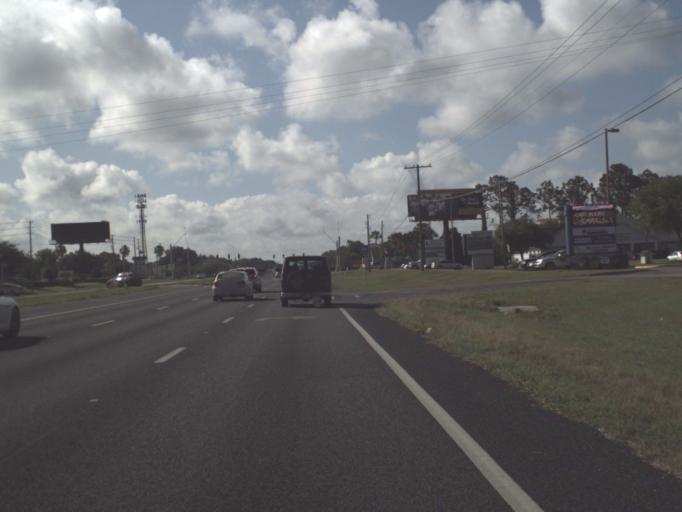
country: US
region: Florida
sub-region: Sumter County
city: The Villages
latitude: 28.9567
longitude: -81.9621
